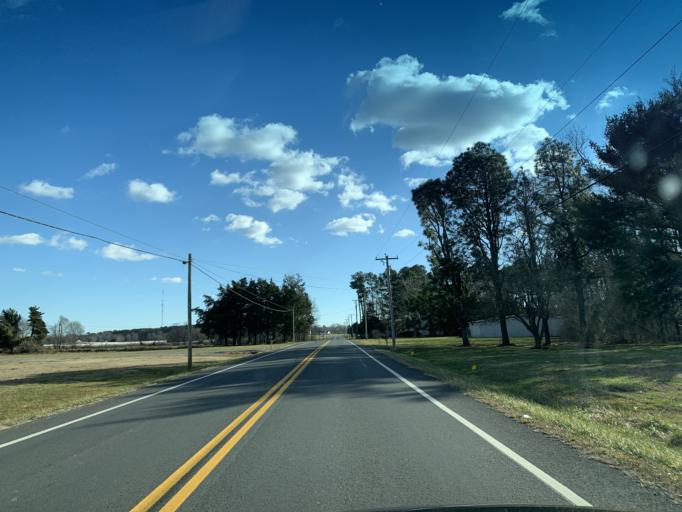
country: US
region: Maryland
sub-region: Worcester County
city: Berlin
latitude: 38.3546
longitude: -75.1958
